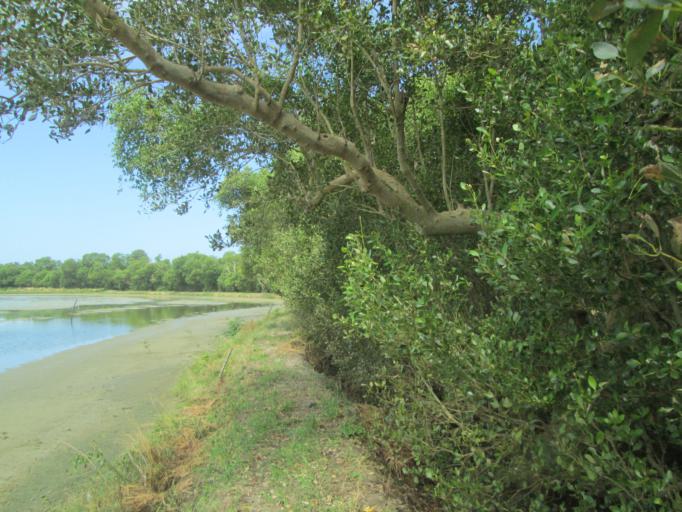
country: PH
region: Ilocos
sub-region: Province of Pangasinan
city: Pangapisan
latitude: 16.2464
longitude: 119.9276
